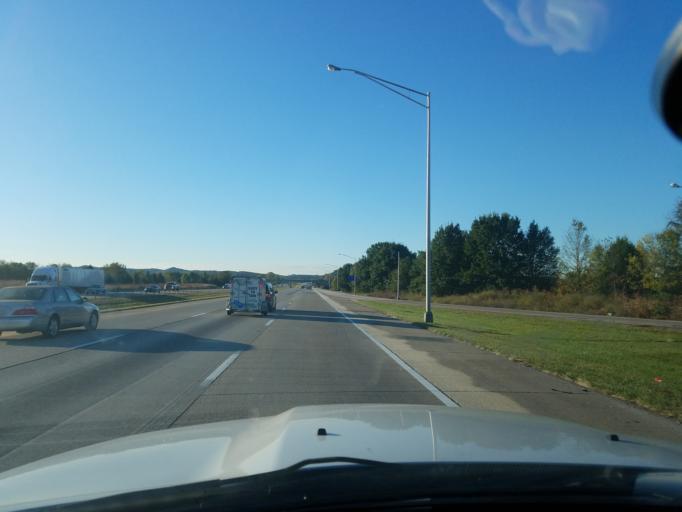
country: US
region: Kentucky
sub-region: Bullitt County
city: Shepherdsville
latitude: 37.9430
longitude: -85.6889
